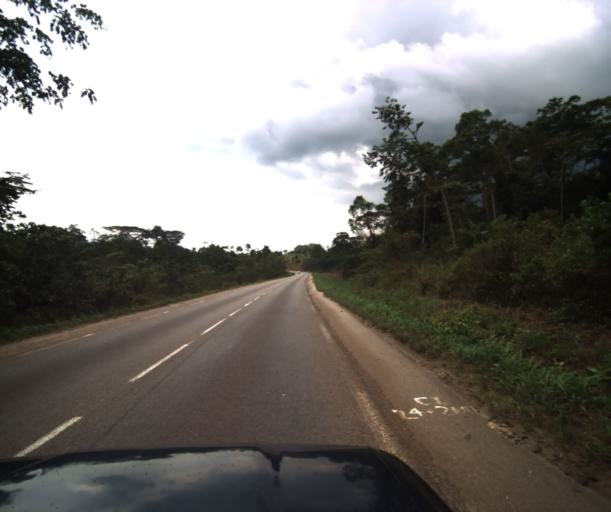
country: CM
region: Littoral
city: Dizangue
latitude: 3.9498
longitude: 10.0180
